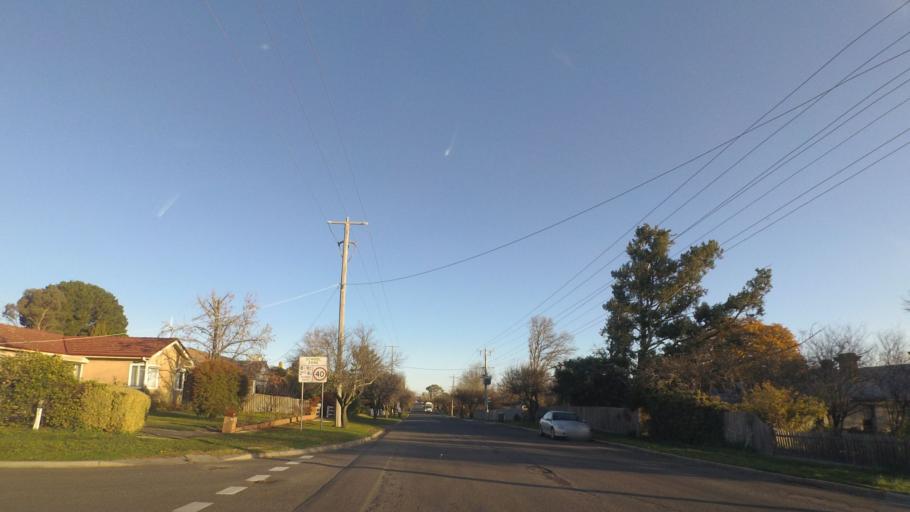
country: AU
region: Victoria
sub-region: Mount Alexander
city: Castlemaine
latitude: -37.2458
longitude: 144.4635
